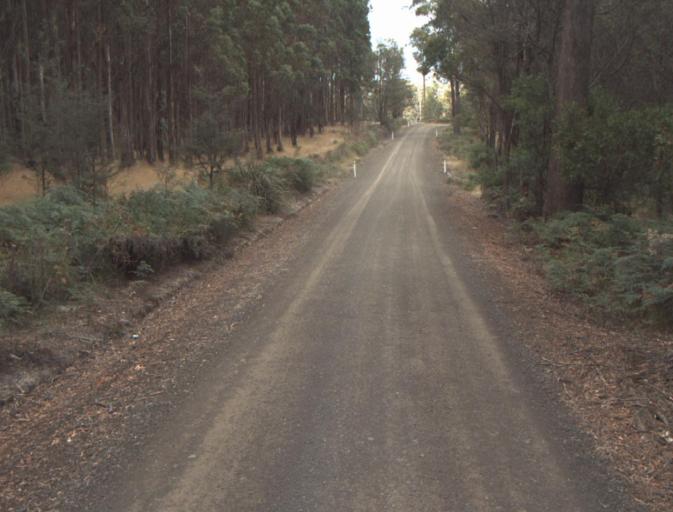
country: AU
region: Tasmania
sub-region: Launceston
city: Mayfield
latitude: -41.2158
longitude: 147.1770
